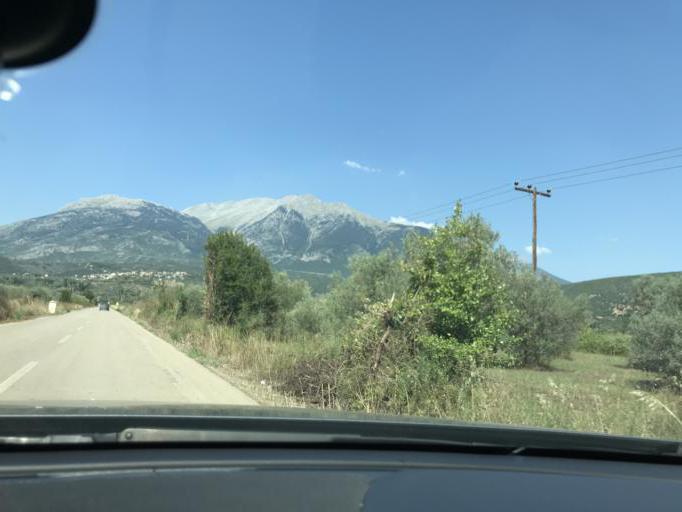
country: GR
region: Central Greece
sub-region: Nomos Fthiotidos
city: Kato Tithorea
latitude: 38.5196
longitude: 22.7646
